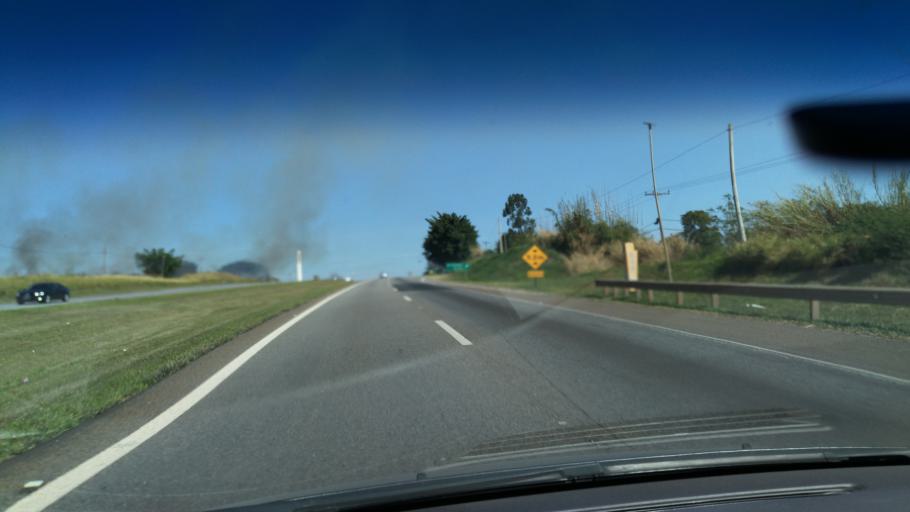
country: BR
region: Sao Paulo
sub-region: Mogi-Mirim
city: Mogi Mirim
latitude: -22.5019
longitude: -46.9851
